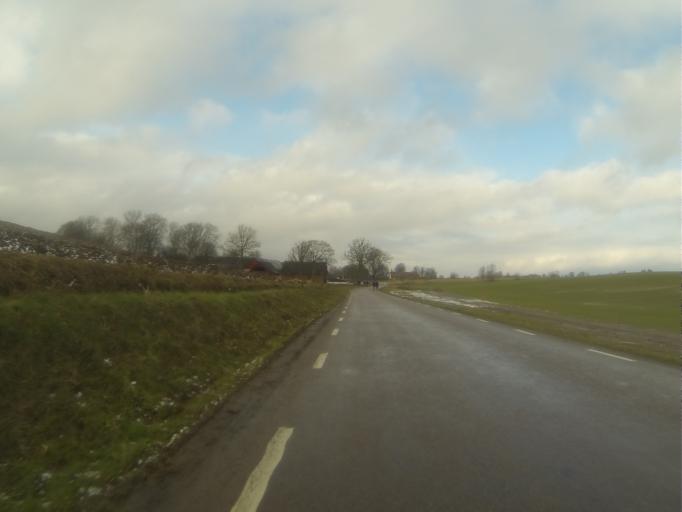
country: SE
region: Skane
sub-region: Svedala Kommun
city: Klagerup
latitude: 55.5810
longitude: 13.2943
